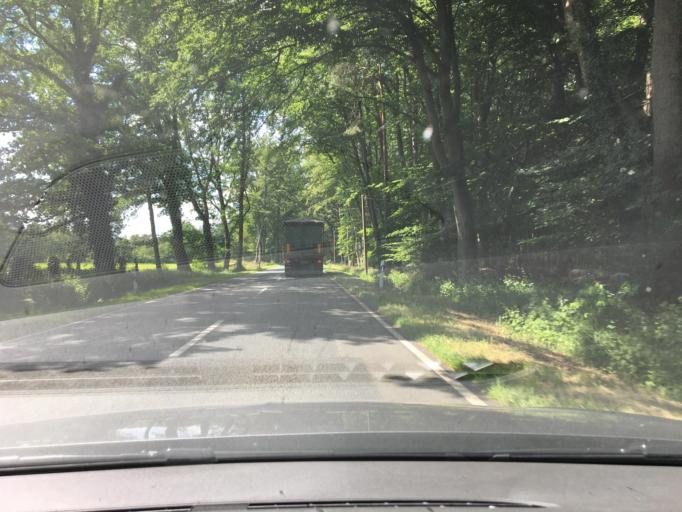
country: DE
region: Lower Saxony
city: Horstedt
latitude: 53.2501
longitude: 9.2247
